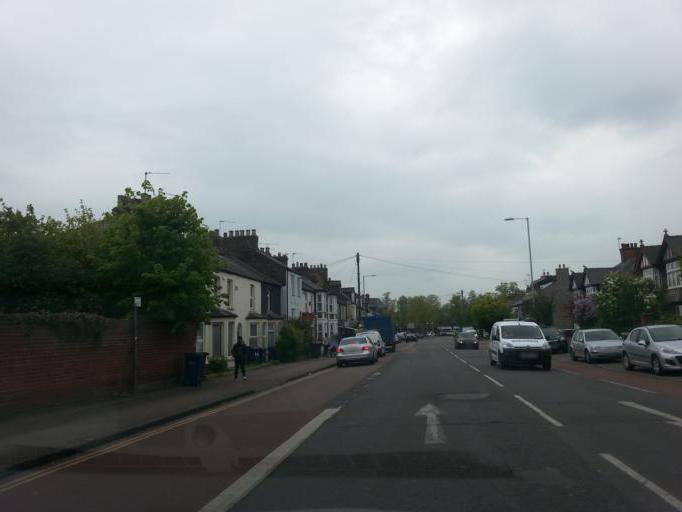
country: GB
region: England
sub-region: Cambridgeshire
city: Cambridge
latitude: 52.2161
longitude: 0.1261
